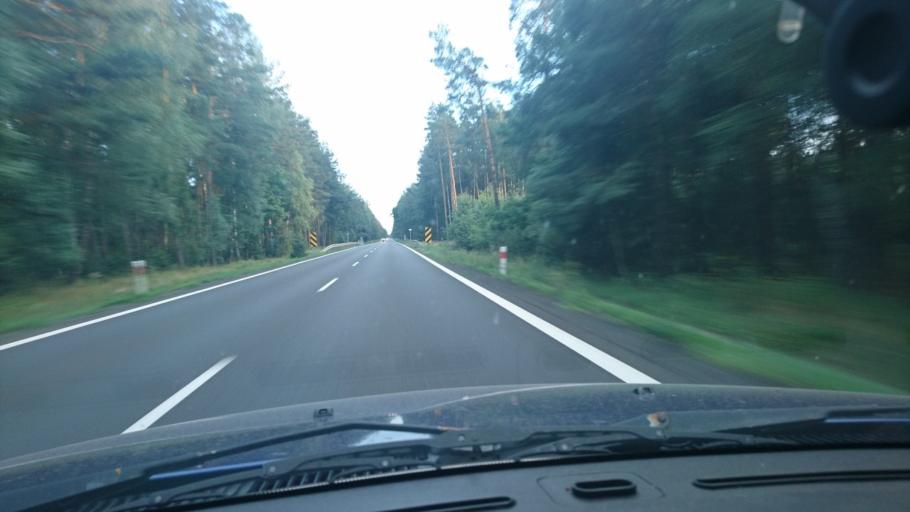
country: PL
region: Silesian Voivodeship
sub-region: Powiat tarnogorski
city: Tworog
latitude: 50.5712
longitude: 18.7106
